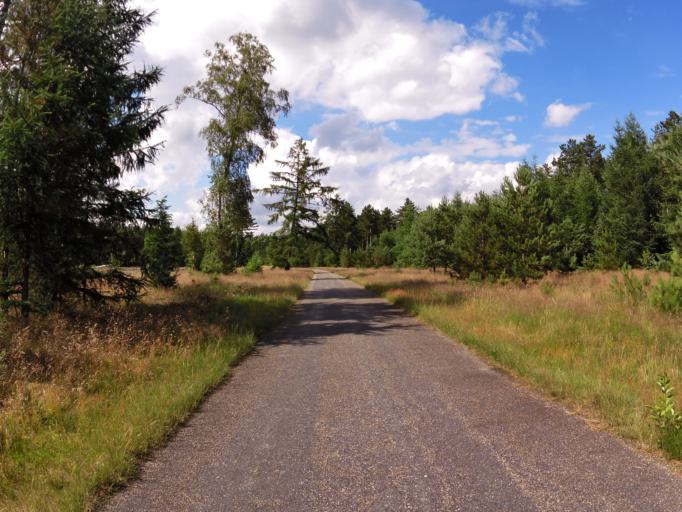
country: NL
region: North Brabant
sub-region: Gemeente Valkenswaard
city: Valkenswaard
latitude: 51.3263
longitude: 5.5111
